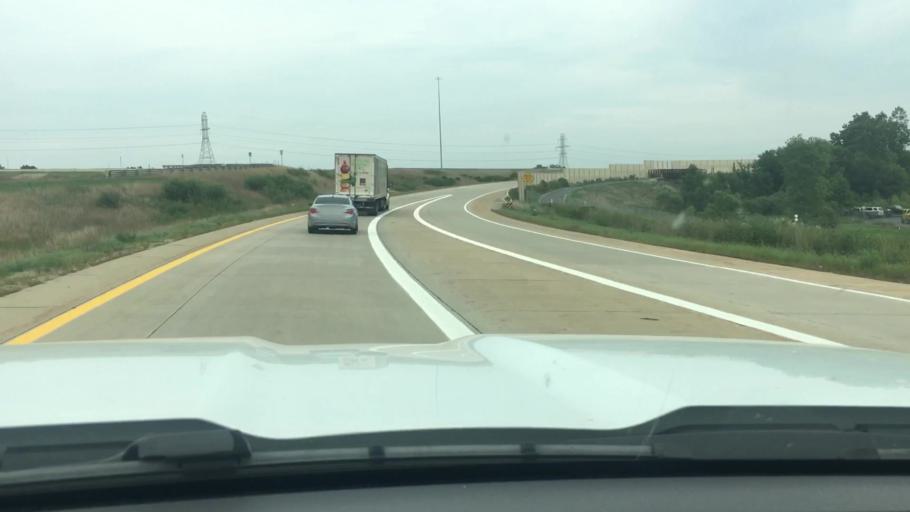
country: US
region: Michigan
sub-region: Kent County
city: Cutlerville
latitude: 42.8459
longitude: -85.6769
